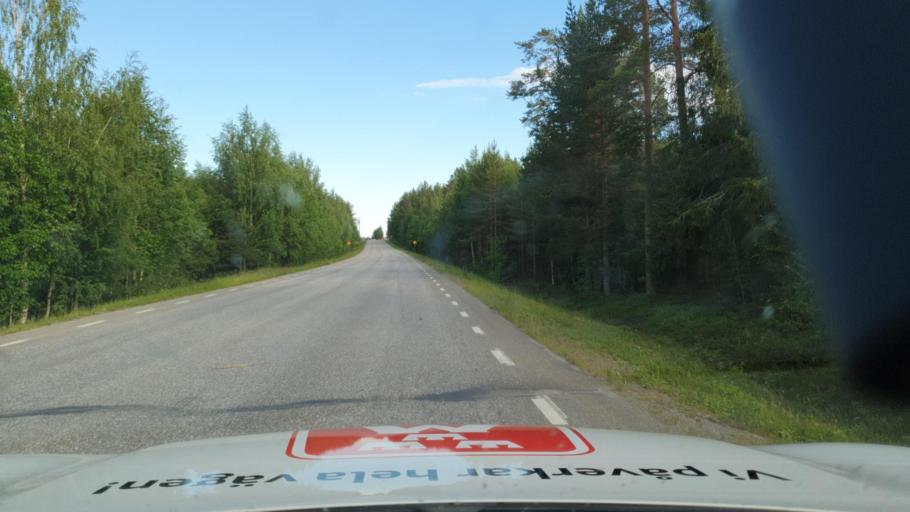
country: SE
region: Vaesterbotten
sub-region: Umea Kommun
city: Roback
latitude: 63.8524
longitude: 20.1512
